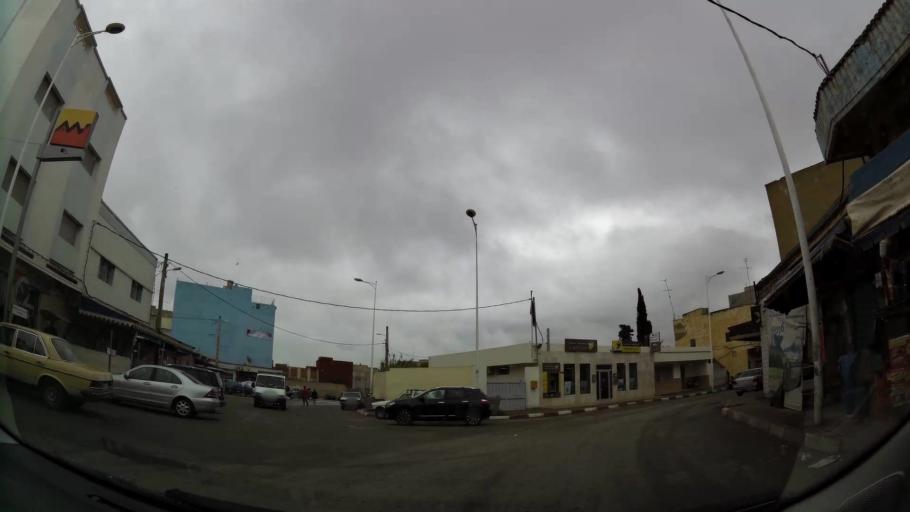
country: MA
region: Oriental
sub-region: Nador
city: Midar
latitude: 35.0455
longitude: -3.4524
